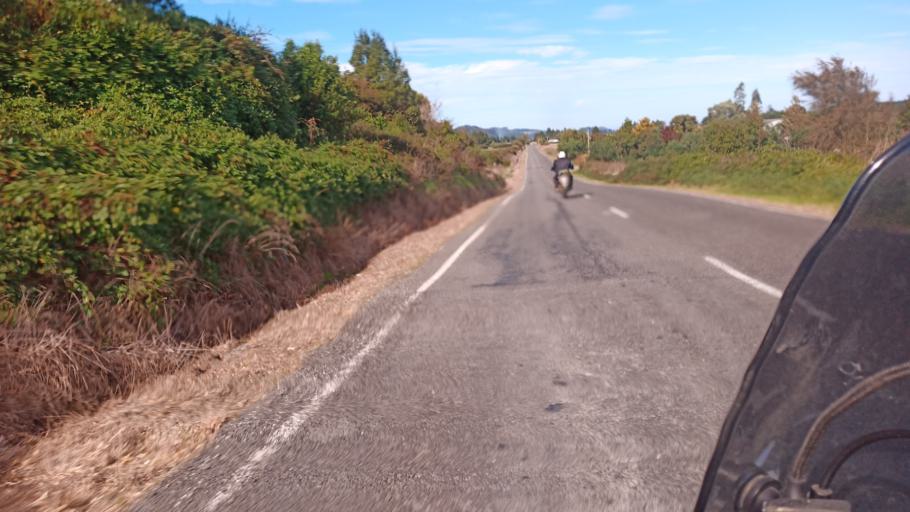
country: NZ
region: Hawke's Bay
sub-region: Wairoa District
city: Wairoa
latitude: -39.0668
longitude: 177.1370
